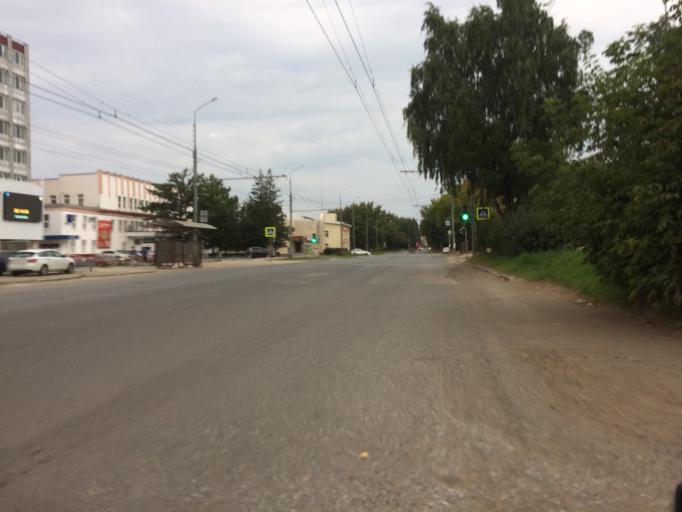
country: RU
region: Mariy-El
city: Yoshkar-Ola
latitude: 56.6339
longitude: 47.8680
